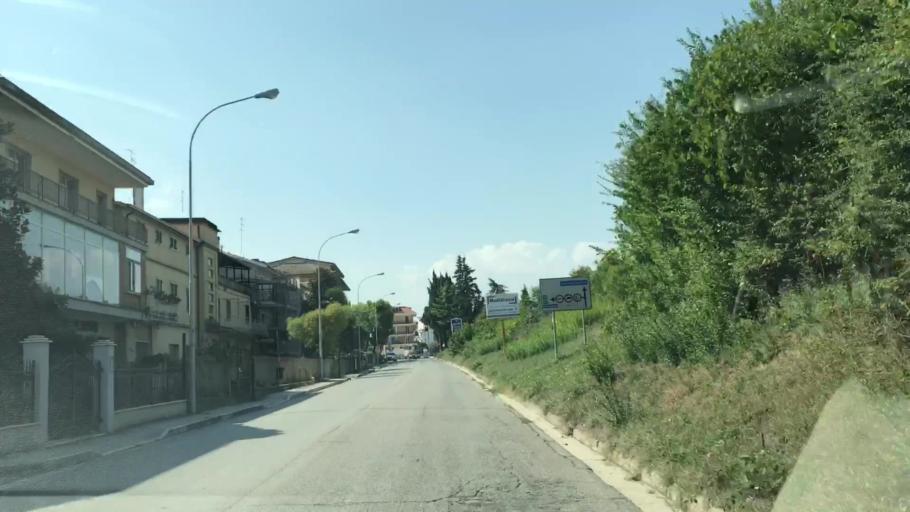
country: IT
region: The Marches
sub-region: Provincia di Ascoli Piceno
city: Stella
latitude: 42.8885
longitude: 13.8179
